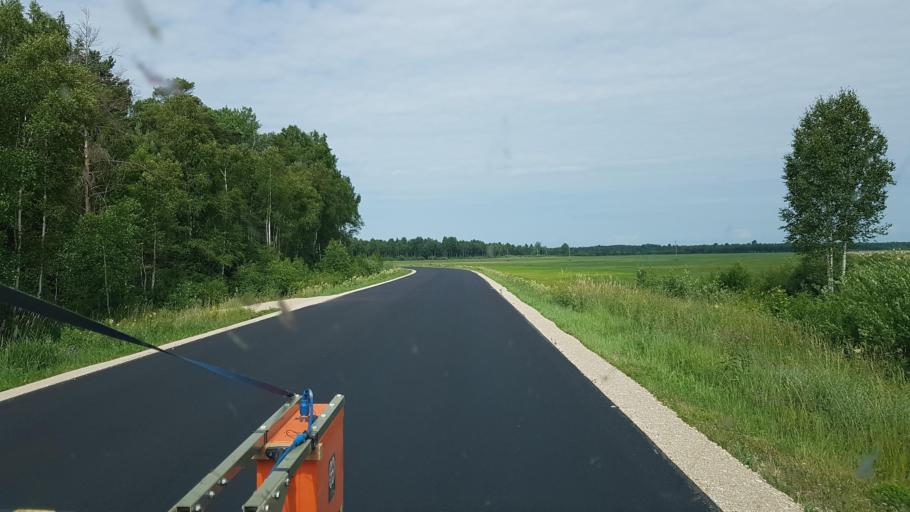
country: EE
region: Paernumaa
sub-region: Halinga vald
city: Parnu-Jaagupi
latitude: 58.6204
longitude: 24.2732
